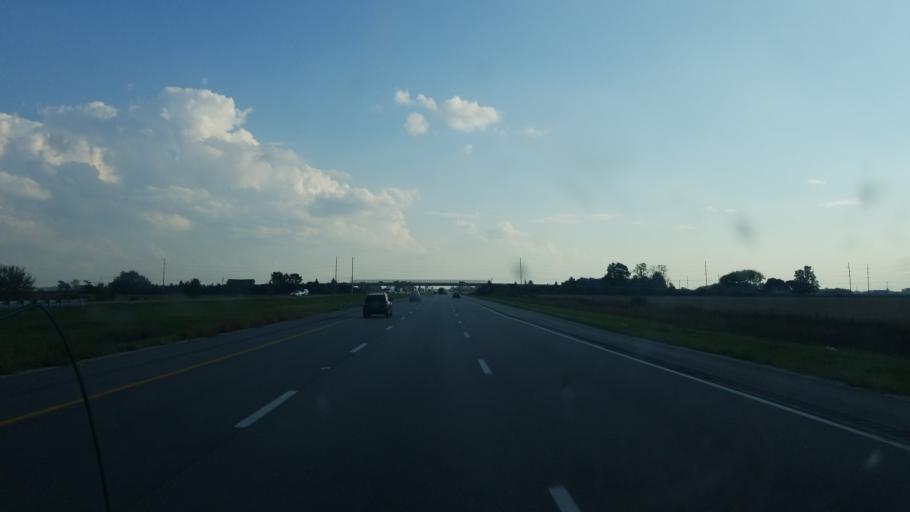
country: US
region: Ohio
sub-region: Wood County
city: Perrysburg
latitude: 41.5260
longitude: -83.6221
